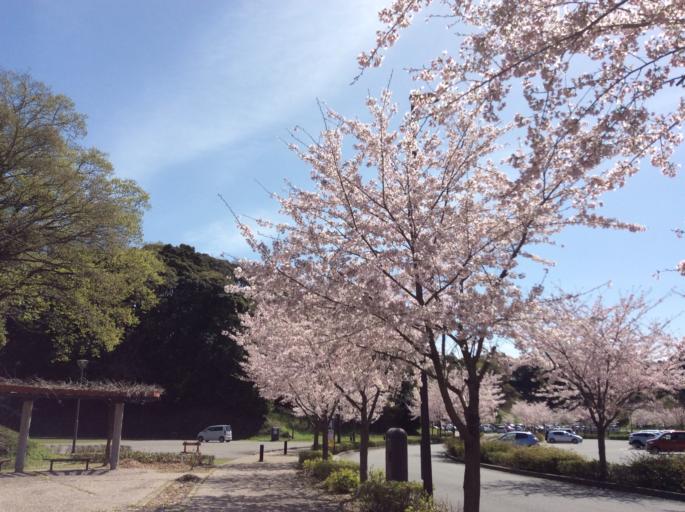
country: JP
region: Shizuoka
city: Kakegawa
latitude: 34.7750
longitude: 138.0581
